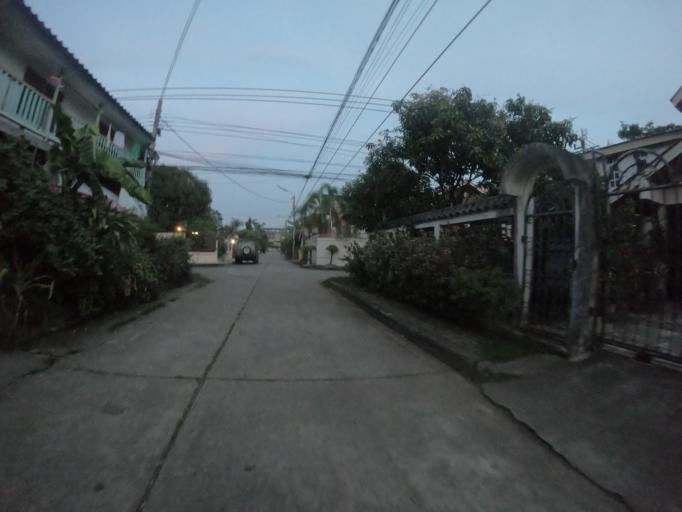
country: TH
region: Bangkok
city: Lat Phrao
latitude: 13.8279
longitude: 100.6123
